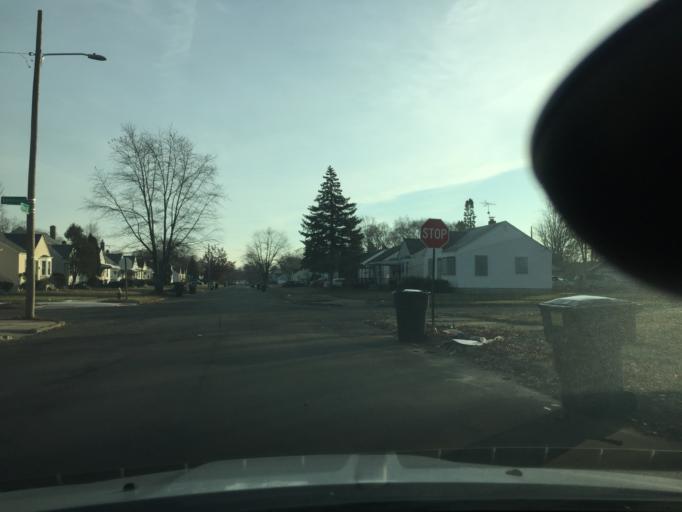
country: US
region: Michigan
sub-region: Macomb County
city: Eastpointe
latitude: 42.4401
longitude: -82.9562
